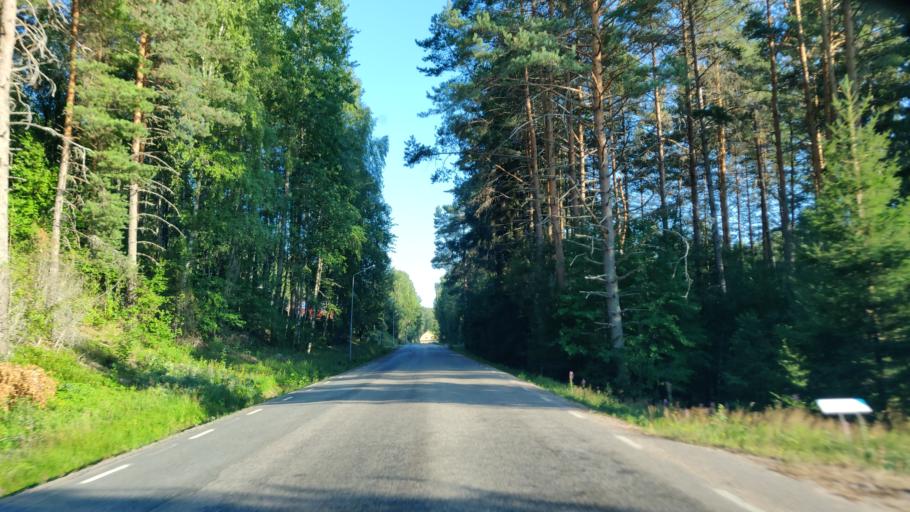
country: SE
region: Vaermland
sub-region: Hagfors Kommun
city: Ekshaerad
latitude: 60.1794
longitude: 13.5266
